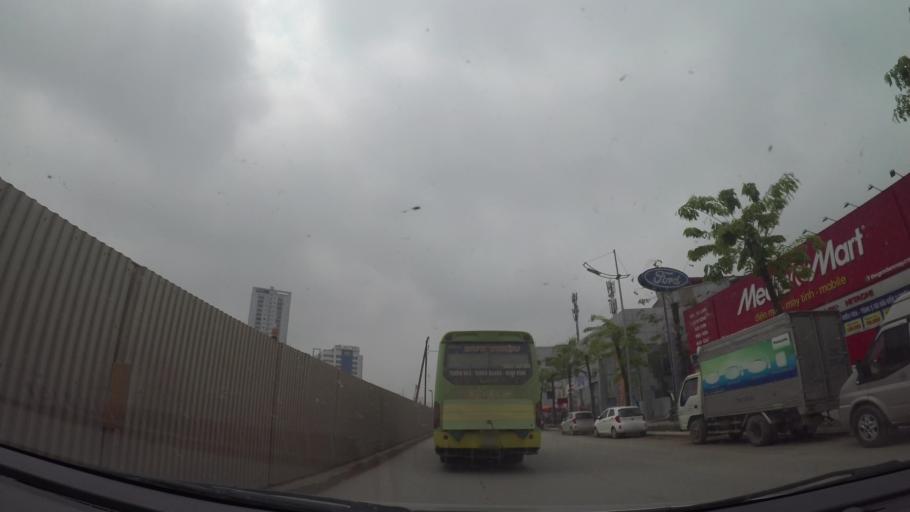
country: VN
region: Ha Noi
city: Tay Ho
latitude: 21.0716
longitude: 105.7854
